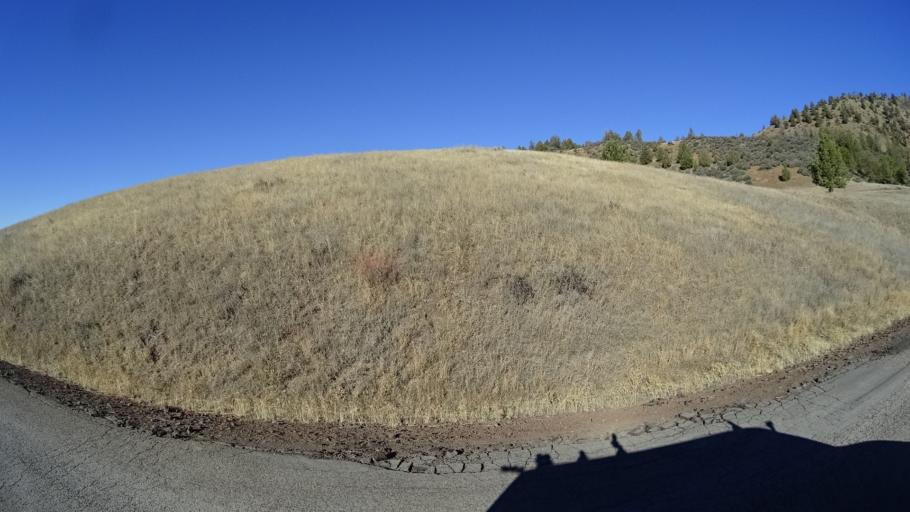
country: US
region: California
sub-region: Siskiyou County
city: Montague
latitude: 41.9689
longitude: -122.4195
